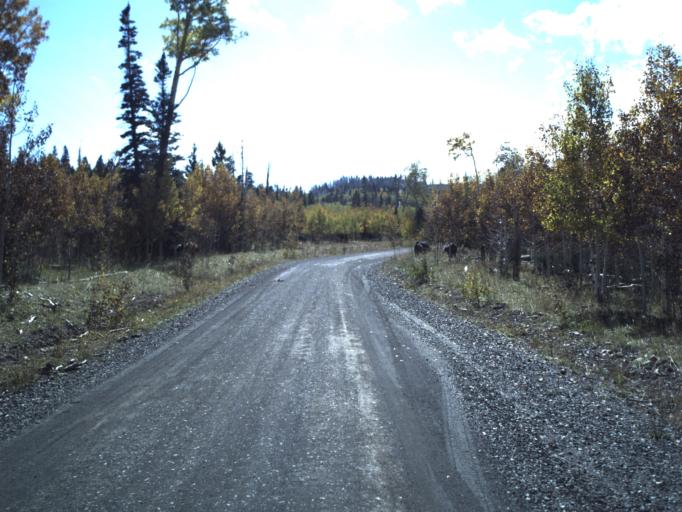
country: US
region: Utah
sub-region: Piute County
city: Junction
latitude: 38.2520
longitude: -112.3363
